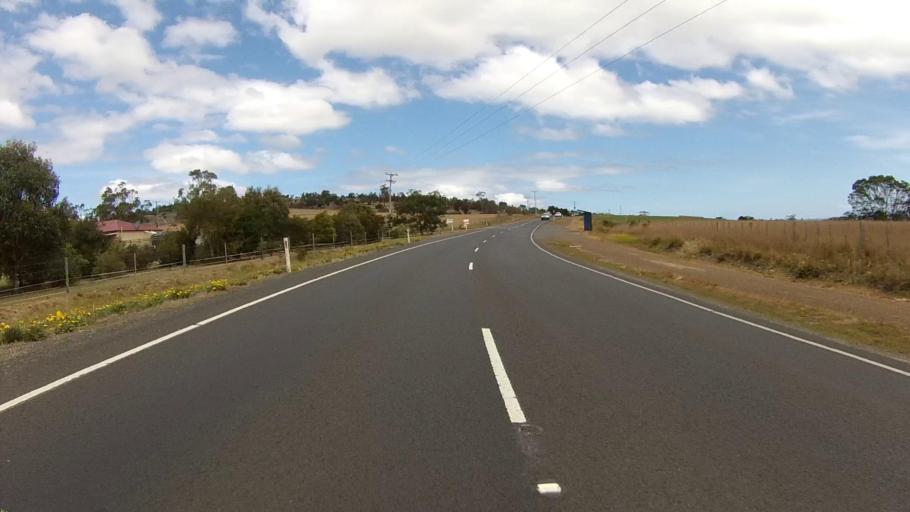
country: AU
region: Tasmania
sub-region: Sorell
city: Sorell
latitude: -42.8324
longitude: 147.6245
